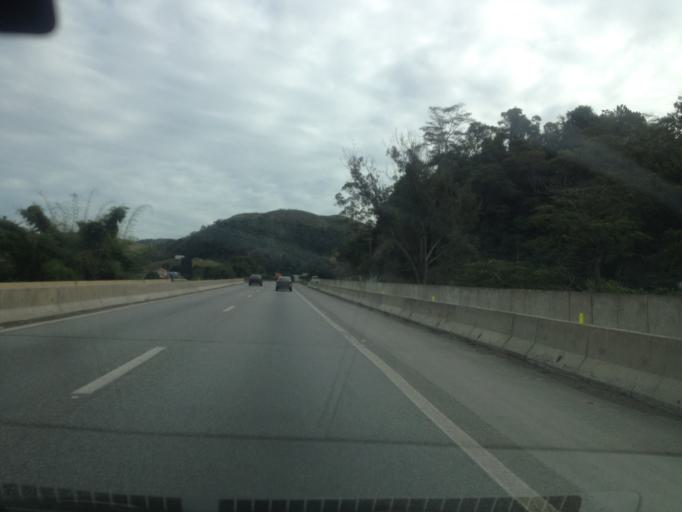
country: BR
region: Rio de Janeiro
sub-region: Pirai
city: Pirai
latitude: -22.6289
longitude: -43.9117
